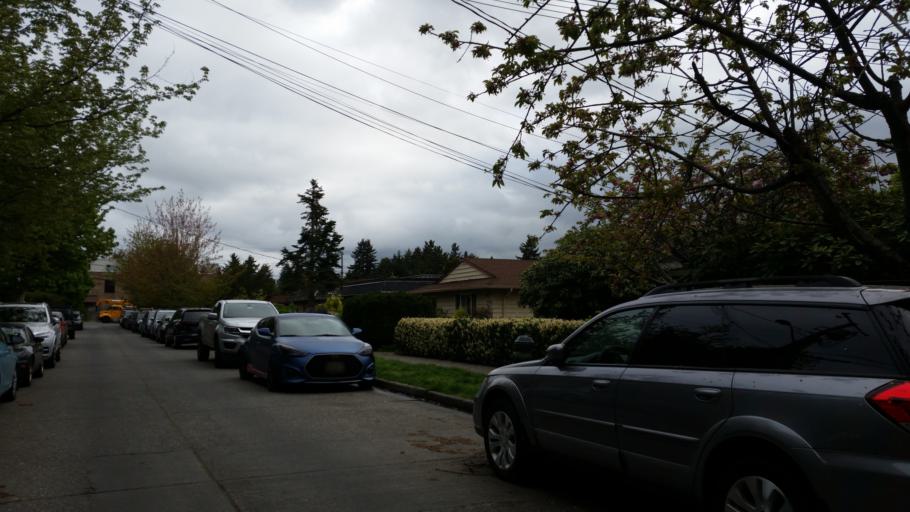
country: US
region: Washington
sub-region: King County
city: Shoreline
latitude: 47.6986
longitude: -122.3408
